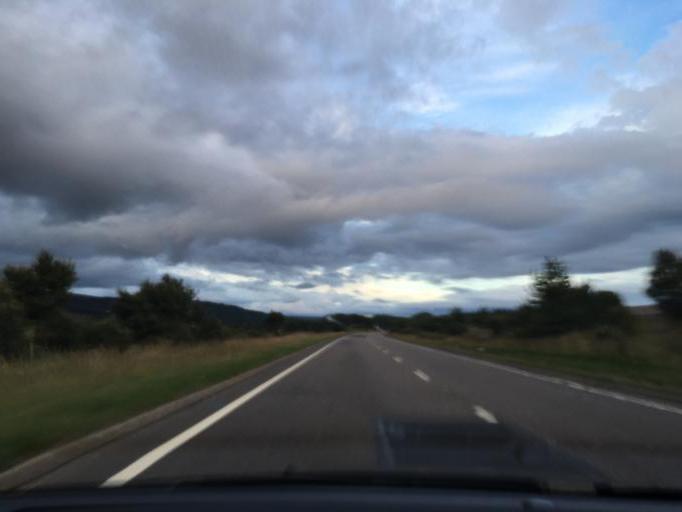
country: GB
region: Scotland
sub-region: Highland
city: Inverness
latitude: 57.3849
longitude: -4.0708
